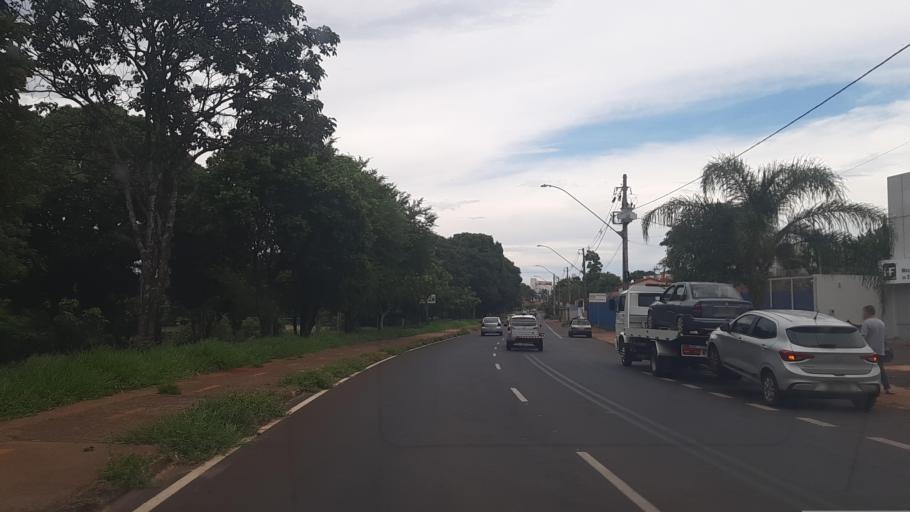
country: BR
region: Minas Gerais
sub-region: Uberlandia
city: Uberlandia
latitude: -18.9250
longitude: -48.2976
